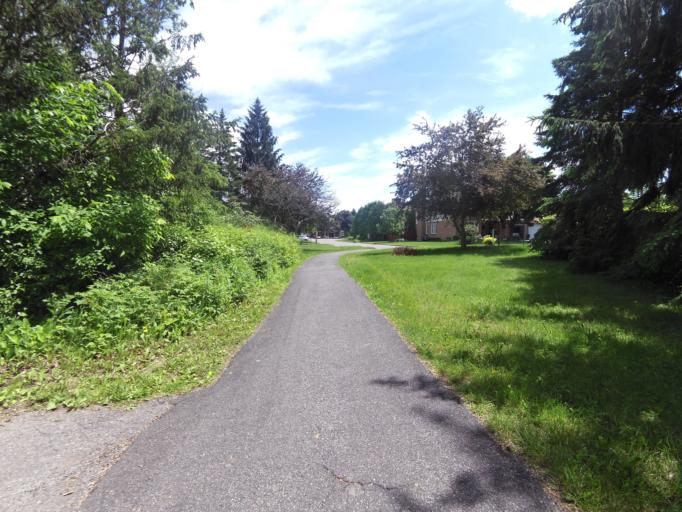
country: CA
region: Ontario
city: Ottawa
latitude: 45.3736
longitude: -75.6134
